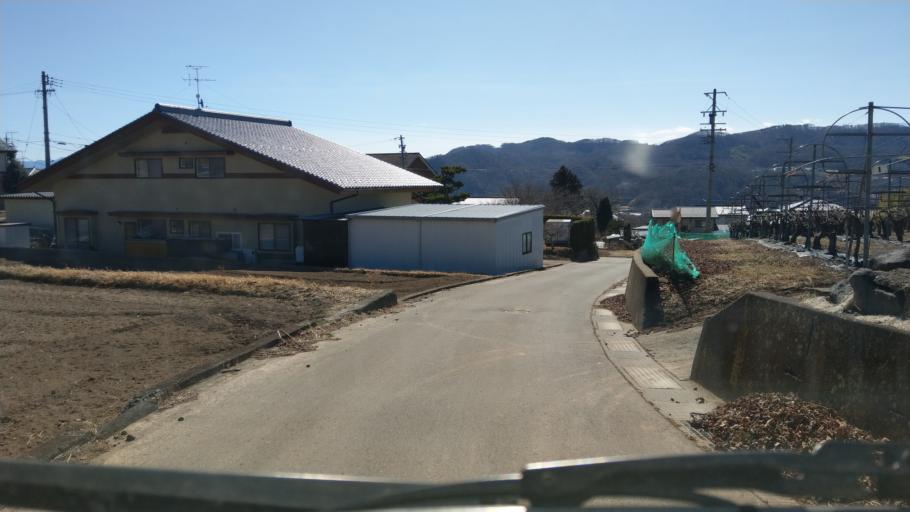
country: JP
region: Nagano
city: Komoro
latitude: 36.3414
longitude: 138.4017
